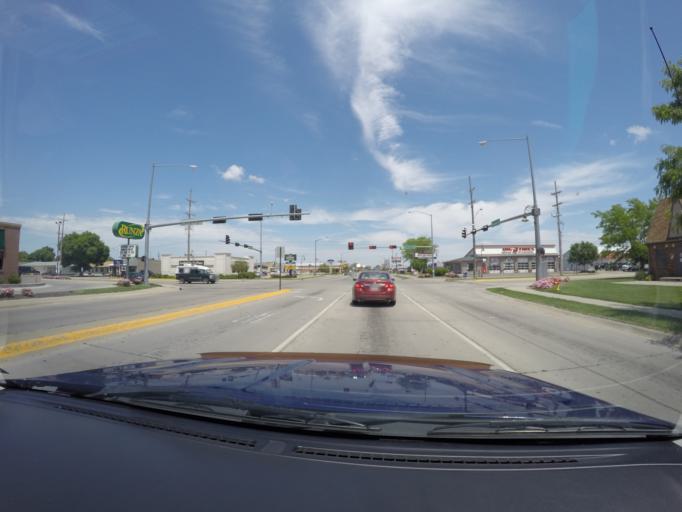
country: US
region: Nebraska
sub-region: Hall County
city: Grand Island
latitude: 40.9018
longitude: -98.3398
